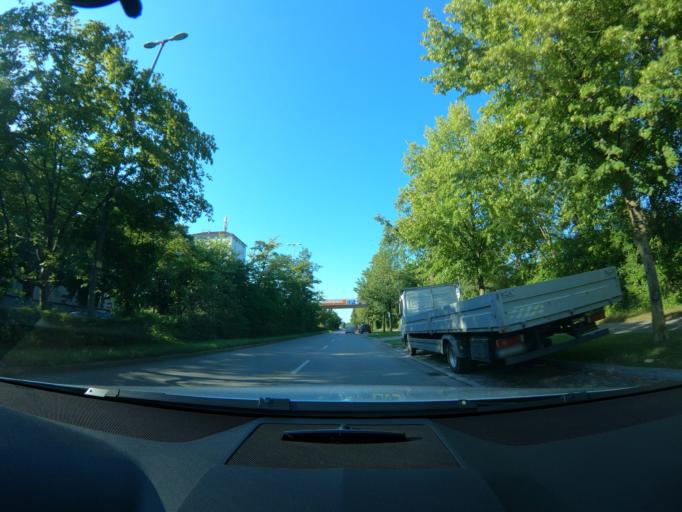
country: DE
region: Bavaria
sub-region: Upper Bavaria
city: Oberschleissheim
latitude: 48.2077
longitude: 11.5868
